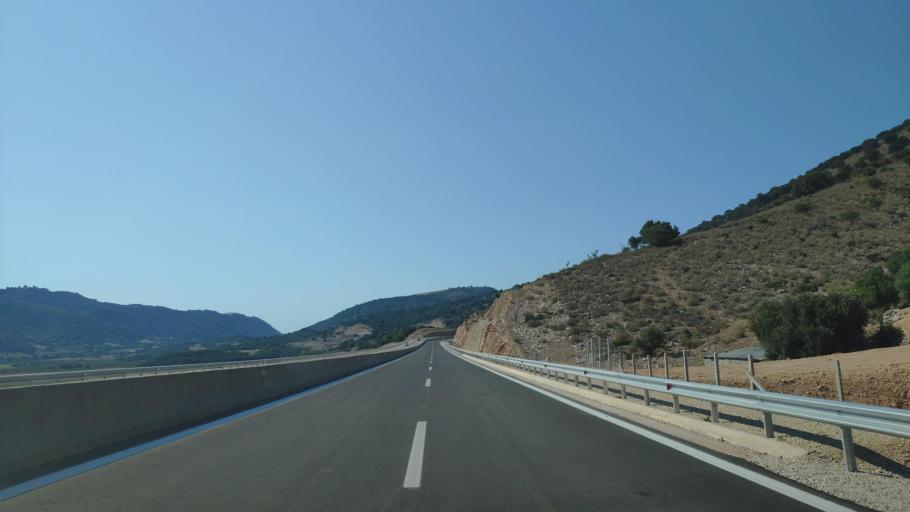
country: GR
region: West Greece
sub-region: Nomos Aitolias kai Akarnanias
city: Katouna
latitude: 38.8299
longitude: 21.1197
